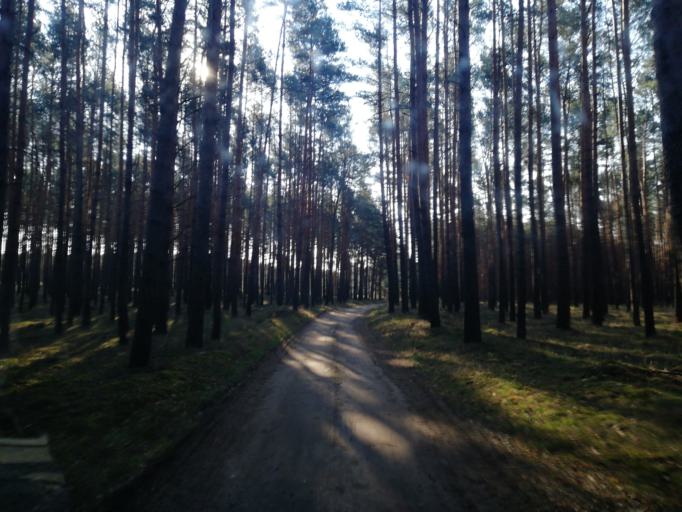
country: DE
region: Brandenburg
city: Drahnsdorf
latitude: 51.9467
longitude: 13.5638
